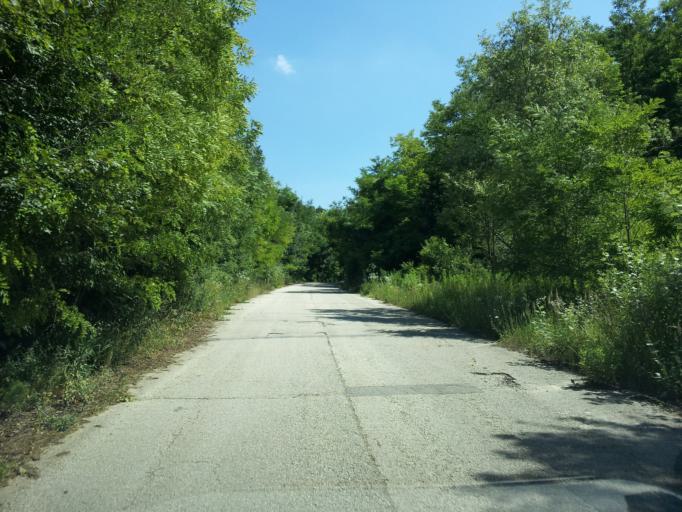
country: HU
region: Fejer
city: Szarliget
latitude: 47.5296
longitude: 18.5538
